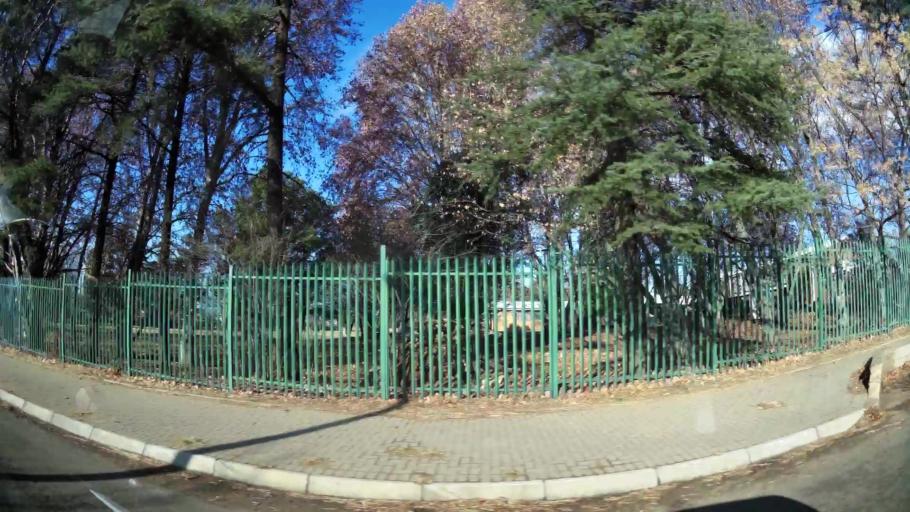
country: ZA
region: Gauteng
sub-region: Sedibeng District Municipality
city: Meyerton
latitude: -26.4915
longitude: 28.0668
